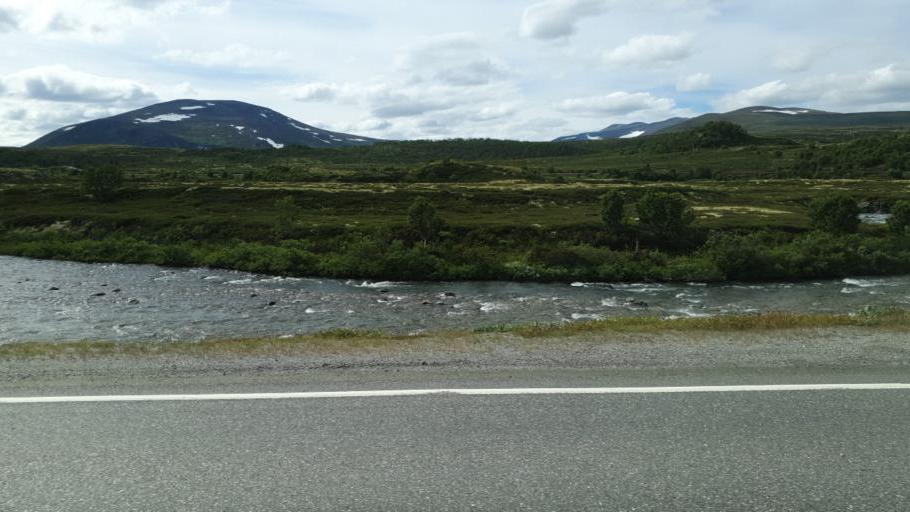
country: NO
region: Sor-Trondelag
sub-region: Oppdal
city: Oppdal
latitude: 62.2802
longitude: 9.5991
